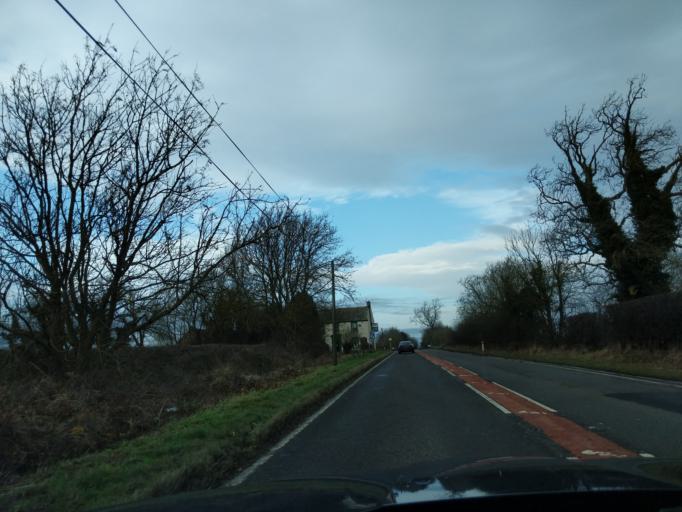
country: GB
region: England
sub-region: Northumberland
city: Meldon
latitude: 55.0835
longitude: -1.8084
